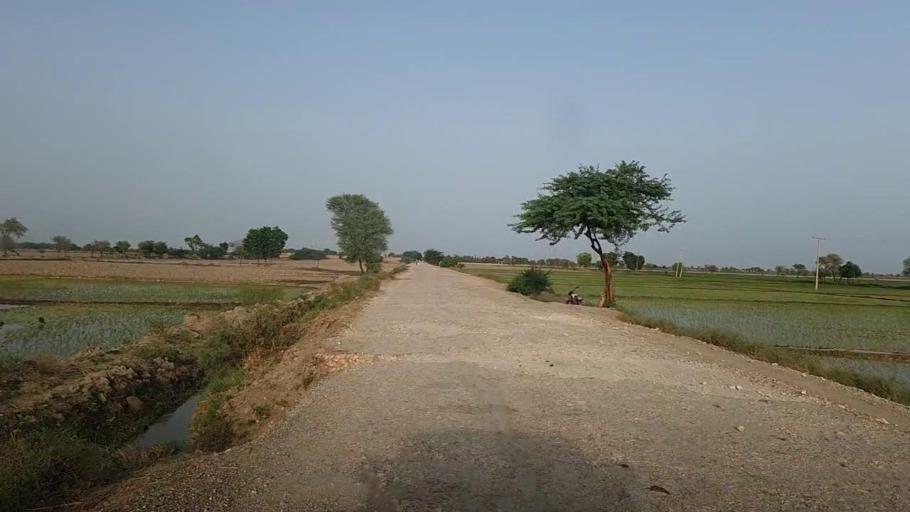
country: PK
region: Sindh
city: Mehar
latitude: 27.1643
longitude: 67.7844
